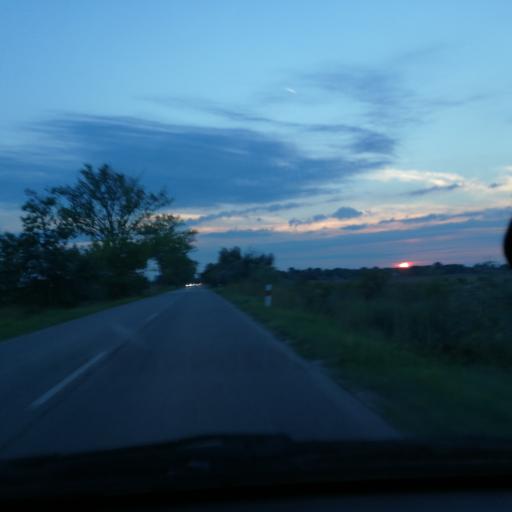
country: HU
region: Bacs-Kiskun
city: Kalocsa
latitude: 46.5092
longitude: 19.0646
